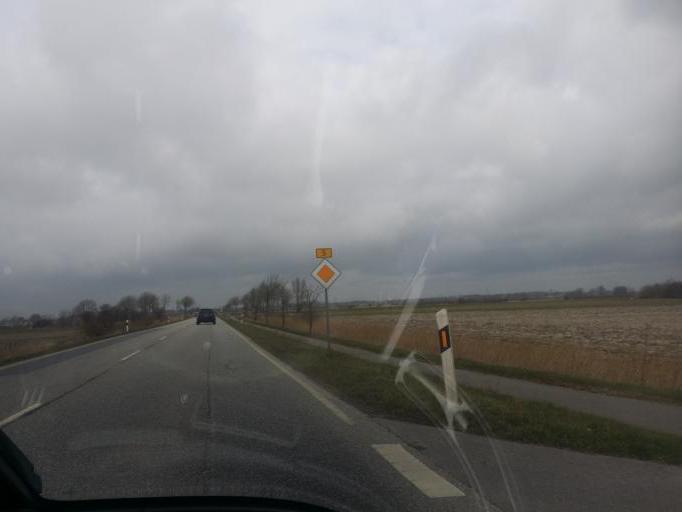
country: DE
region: Schleswig-Holstein
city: Hattstedtermarsch
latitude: 54.5634
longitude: 9.0003
